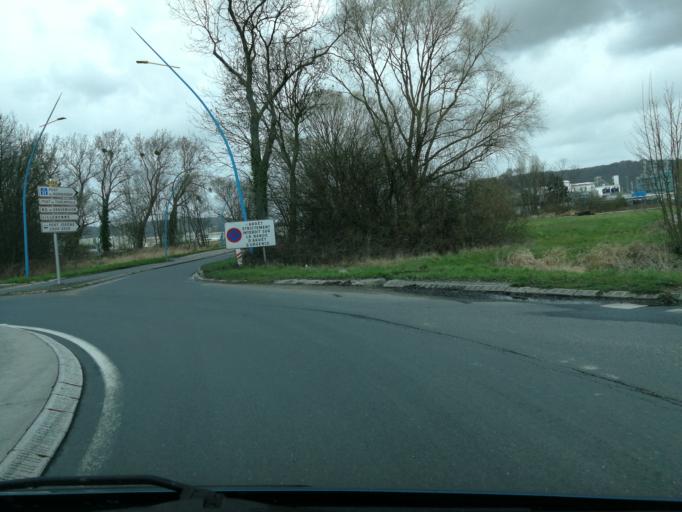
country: FR
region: Haute-Normandie
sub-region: Departement de l'Eure
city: Quillebeuf-sur-Seine
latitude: 49.4837
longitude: 0.5317
